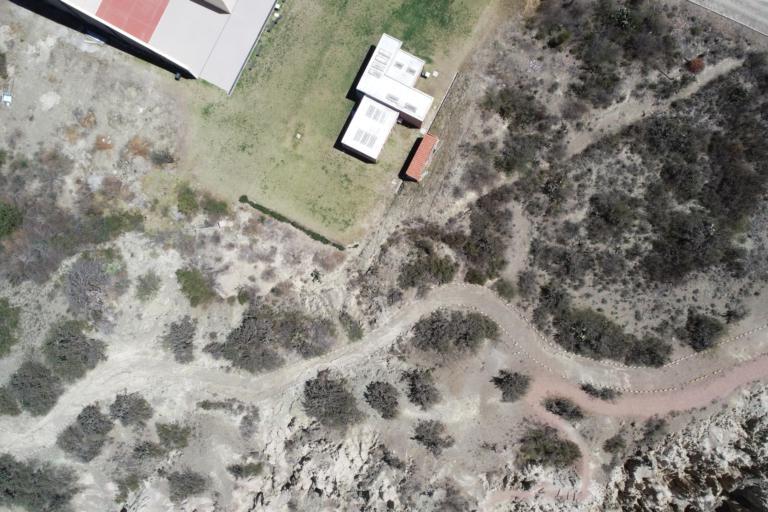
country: BO
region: La Paz
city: La Paz
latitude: -16.6270
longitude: -68.0567
